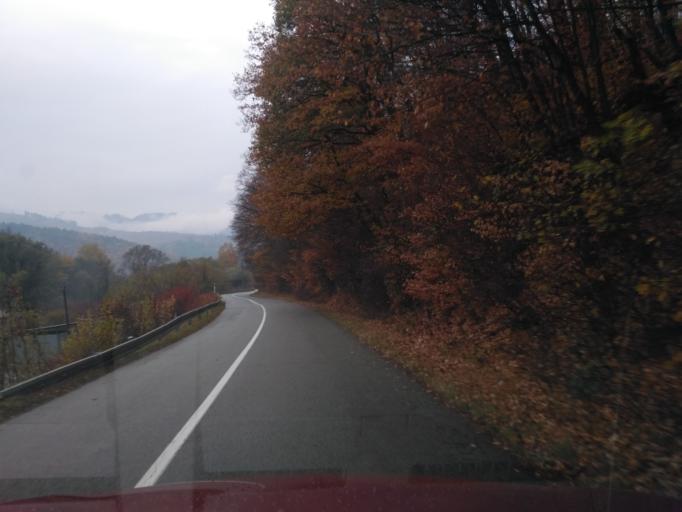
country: SK
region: Kosicky
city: Medzev
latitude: 48.7084
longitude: 20.8023
